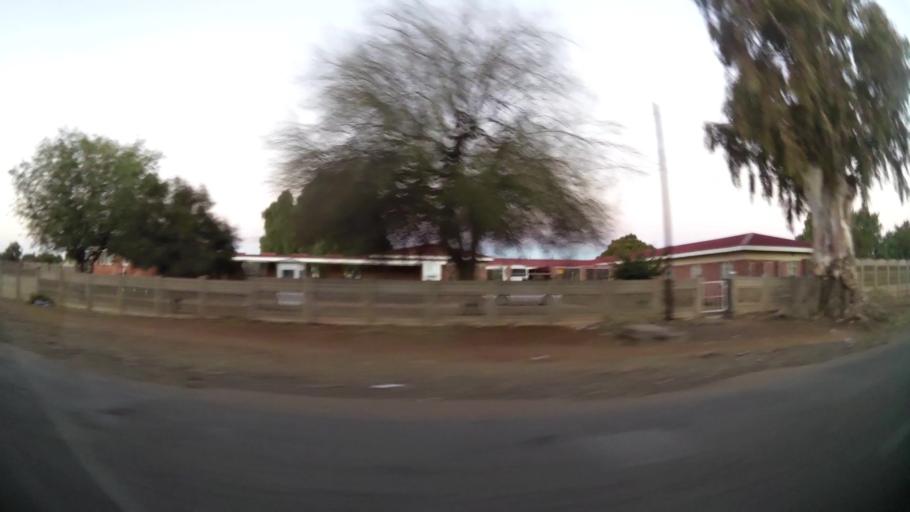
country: ZA
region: Northern Cape
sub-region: Frances Baard District Municipality
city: Kimberley
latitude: -28.7236
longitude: 24.7670
